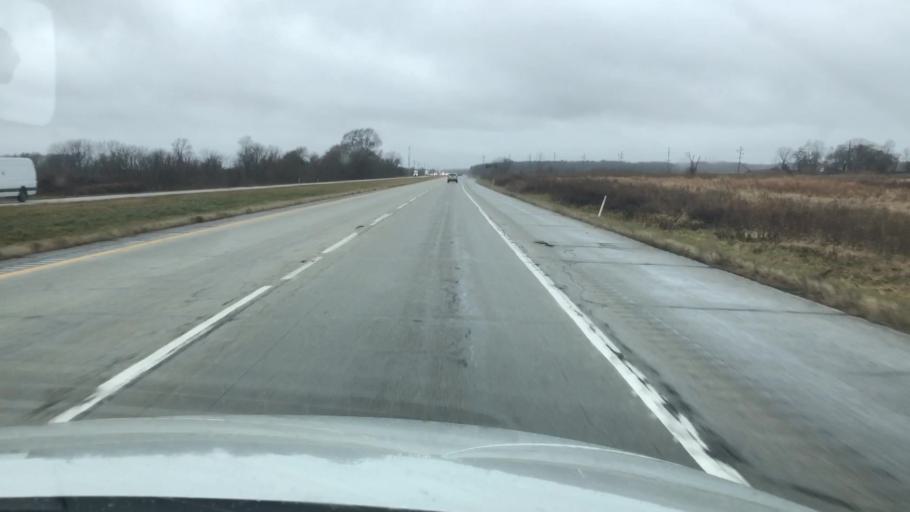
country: US
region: Indiana
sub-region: Starke County
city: Koontz Lake
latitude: 41.3735
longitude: -86.5201
